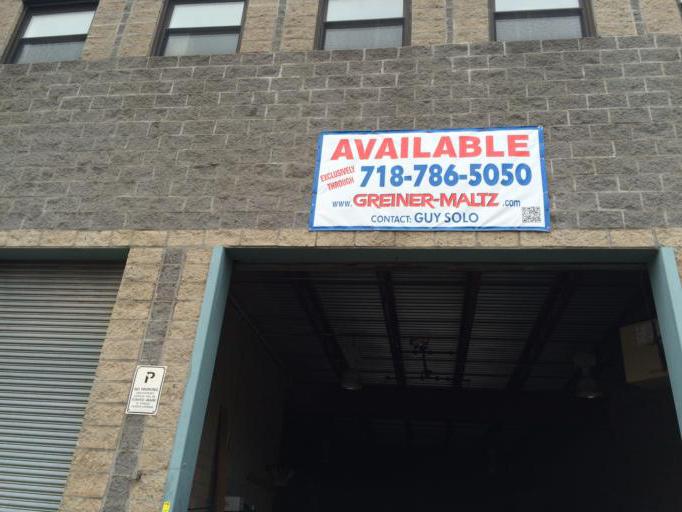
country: US
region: New York
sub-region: Kings County
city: Bensonhurst
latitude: 40.6474
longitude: -74.0172
